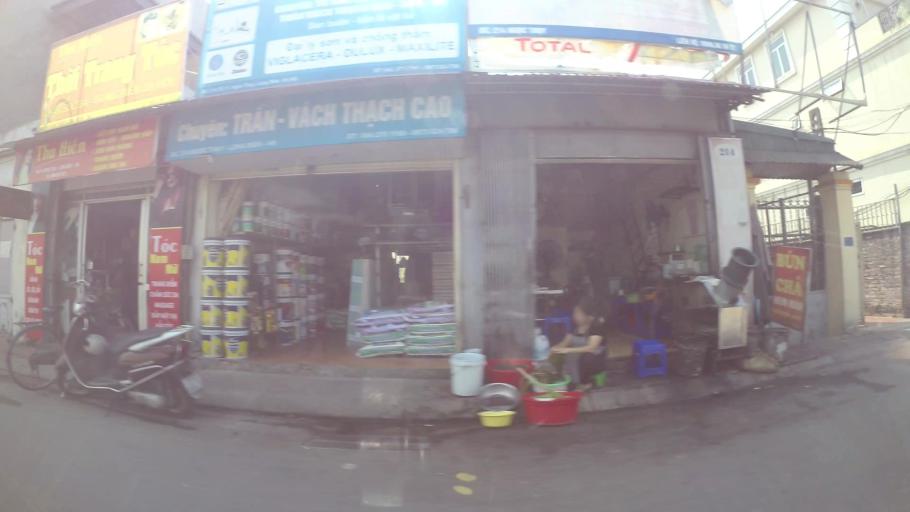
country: VN
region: Ha Noi
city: Hoan Kiem
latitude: 21.0544
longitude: 105.8651
